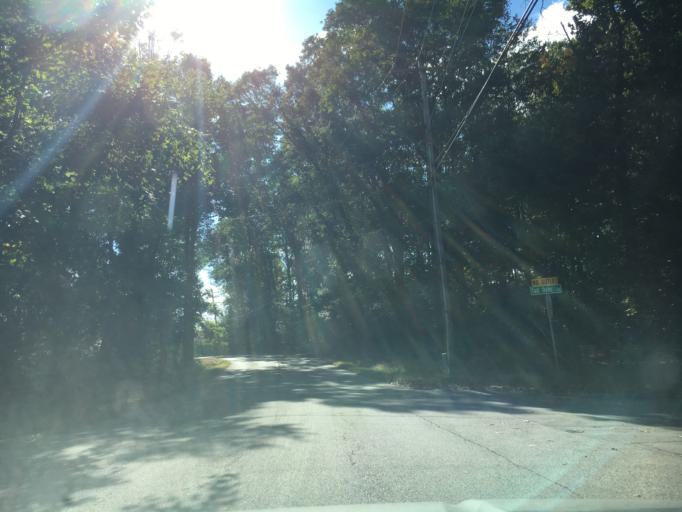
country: US
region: Pennsylvania
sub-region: York County
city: Yorklyn
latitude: 40.0066
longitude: -76.6695
